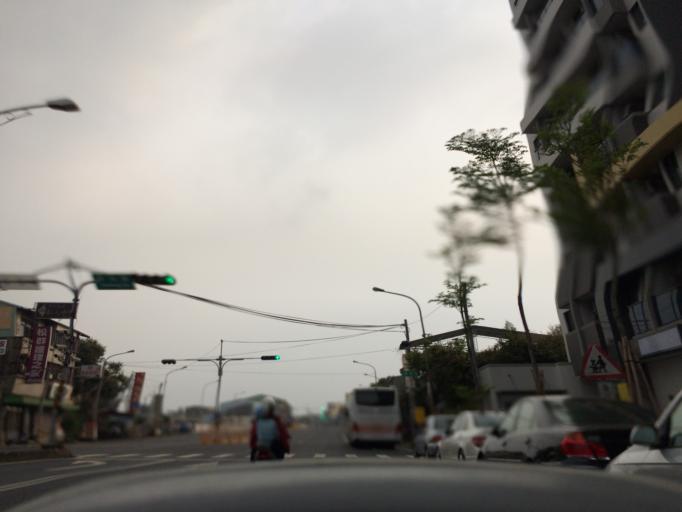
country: TW
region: Taiwan
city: Zhongxing New Village
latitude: 24.0453
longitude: 120.6922
